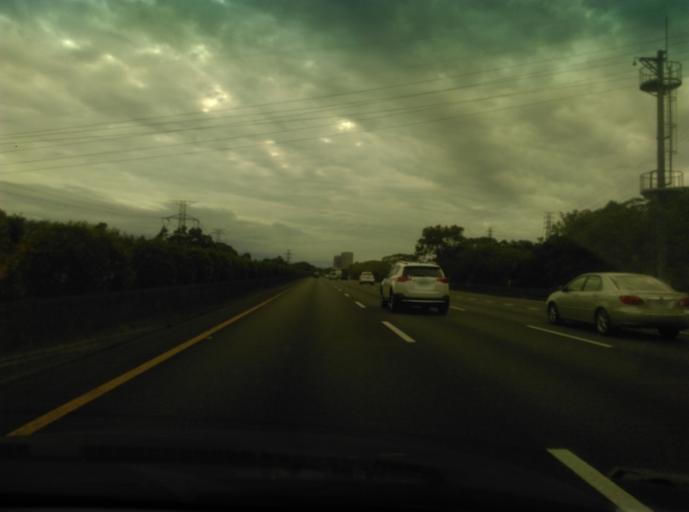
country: TW
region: Taiwan
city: Daxi
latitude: 24.9163
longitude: 121.2950
